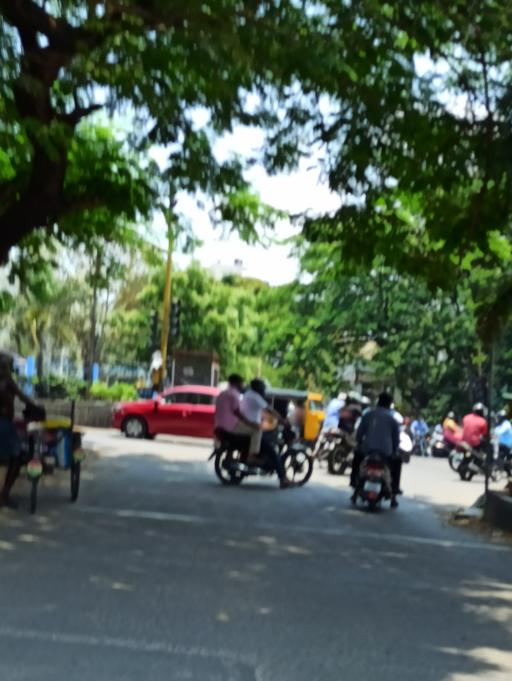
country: IN
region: Tamil Nadu
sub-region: Chennai
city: Chetput
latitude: 13.0888
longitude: 80.2315
